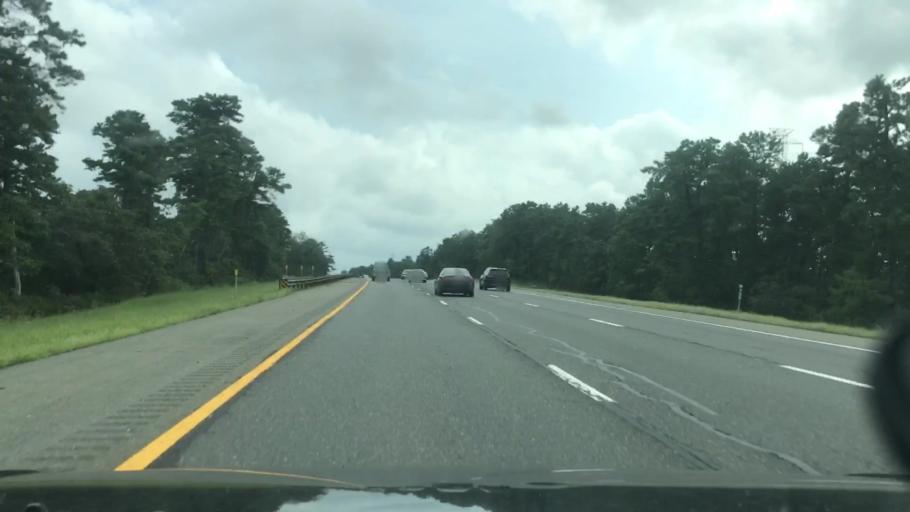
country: US
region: New Jersey
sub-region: Ocean County
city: Forked River
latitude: 39.8286
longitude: -74.2275
